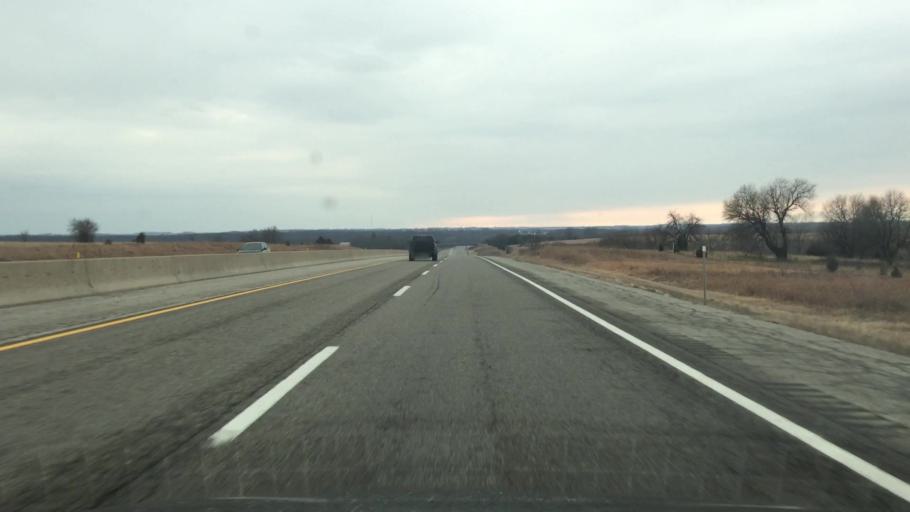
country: US
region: Kansas
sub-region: Shawnee County
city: Auburn
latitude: 38.9059
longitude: -95.7914
